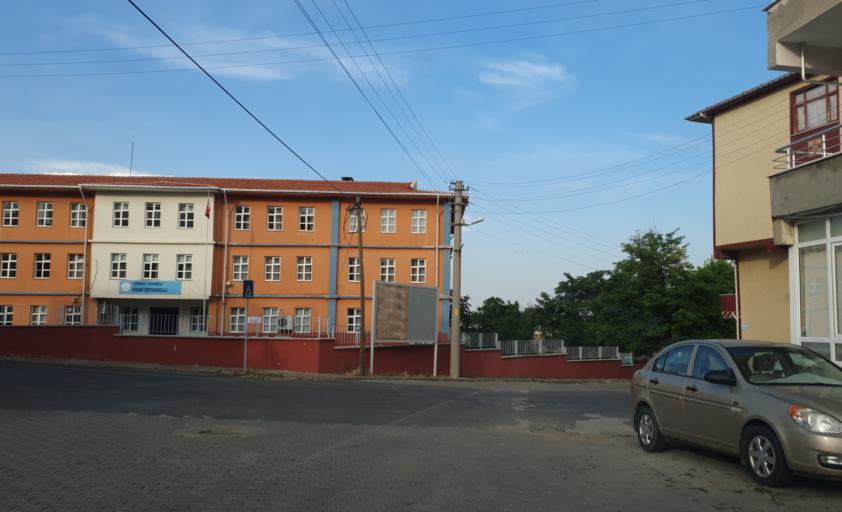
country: TR
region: Tekirdag
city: Hayrabolu
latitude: 41.2131
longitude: 27.1103
